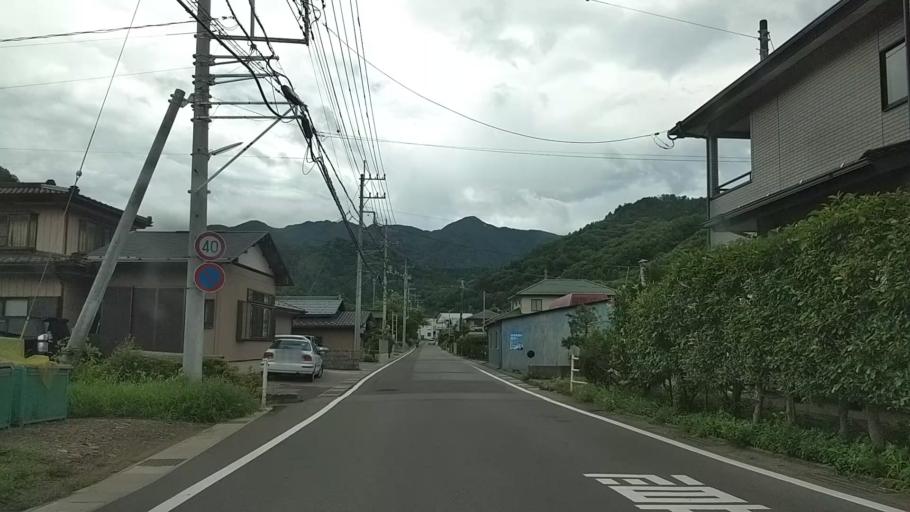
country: JP
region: Yamanashi
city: Otsuki
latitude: 35.5686
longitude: 138.9326
